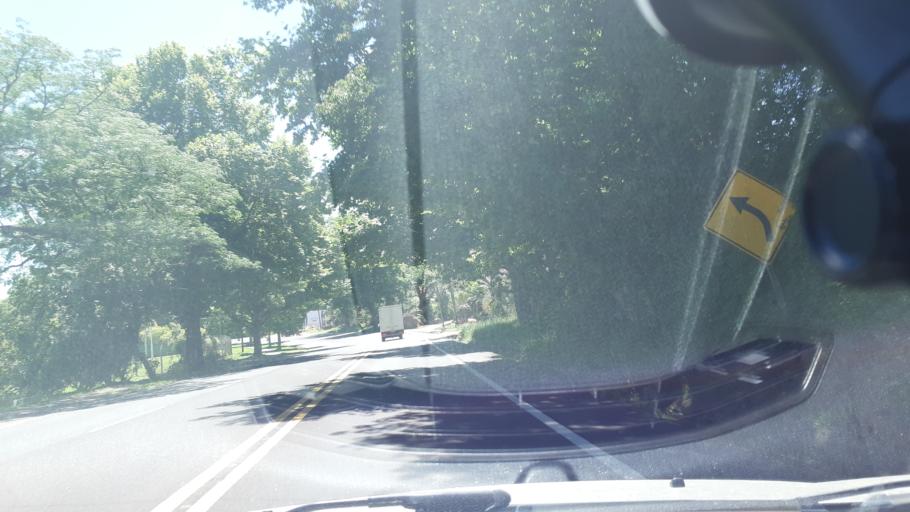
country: BR
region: Rio Grande do Sul
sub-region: Ivoti
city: Ivoti
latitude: -29.6203
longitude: -51.1241
